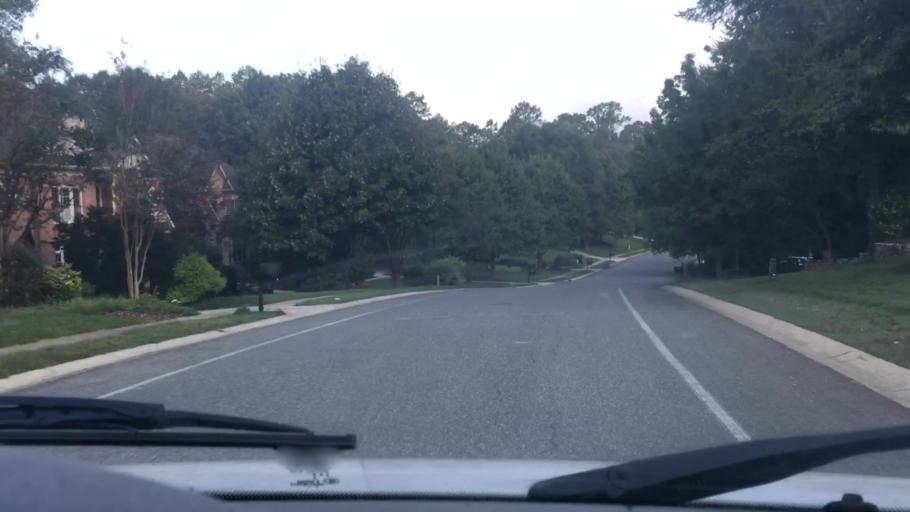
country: US
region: North Carolina
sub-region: Gaston County
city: Davidson
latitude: 35.4693
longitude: -80.8090
